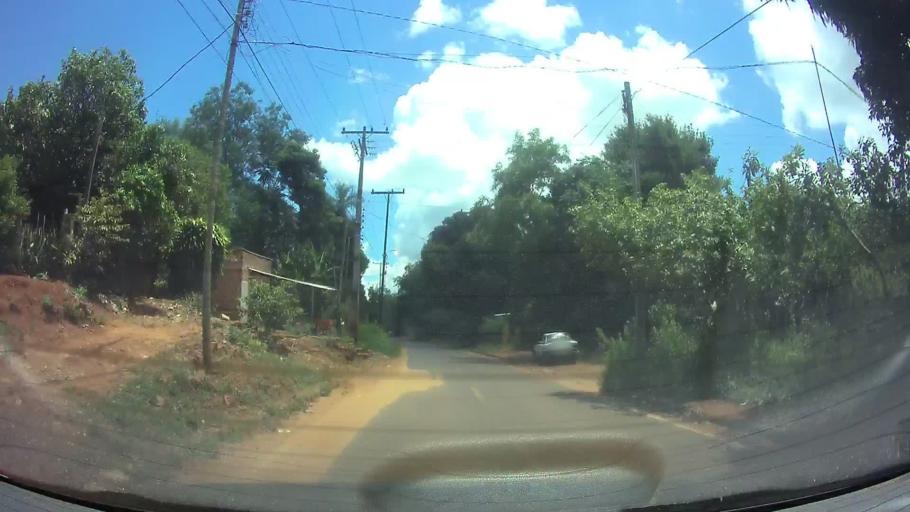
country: PY
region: Central
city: Itaugua
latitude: -25.3824
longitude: -57.3661
